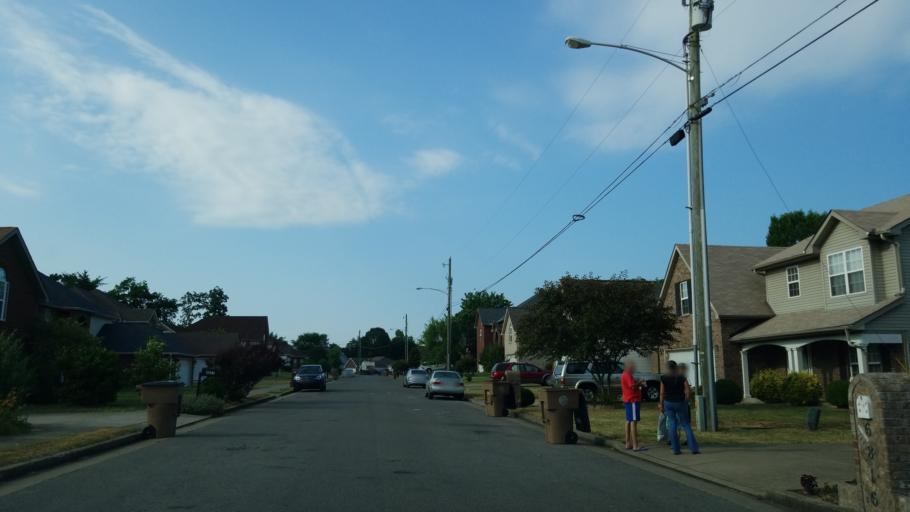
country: US
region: Tennessee
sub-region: Rutherford County
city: La Vergne
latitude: 36.0343
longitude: -86.5839
